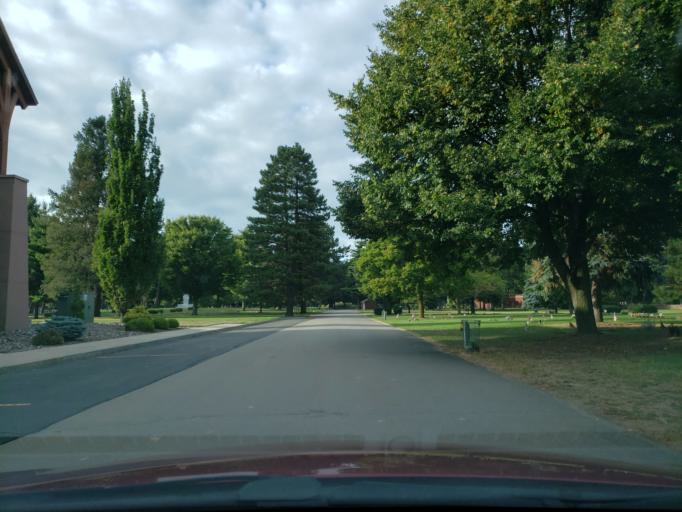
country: US
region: New York
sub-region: Monroe County
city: Irondequoit
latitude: 43.2113
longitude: -77.6312
